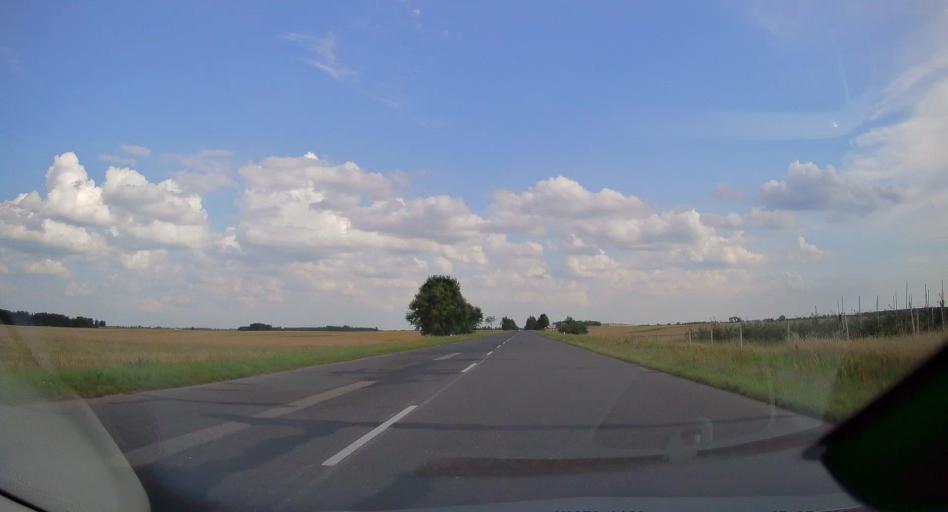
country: PL
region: Lodz Voivodeship
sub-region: Powiat tomaszowski
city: Rzeczyca
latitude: 51.6593
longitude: 20.2713
